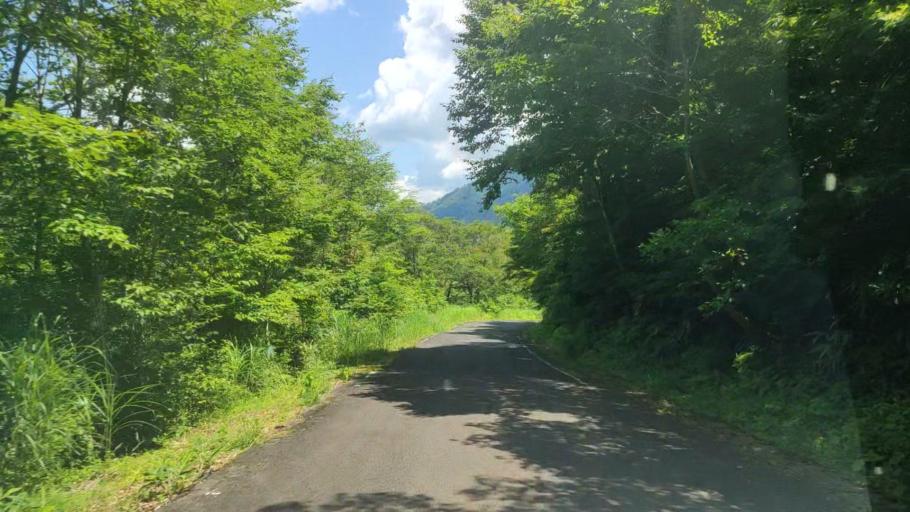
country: JP
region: Fukui
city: Ono
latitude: 35.7768
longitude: 136.5233
